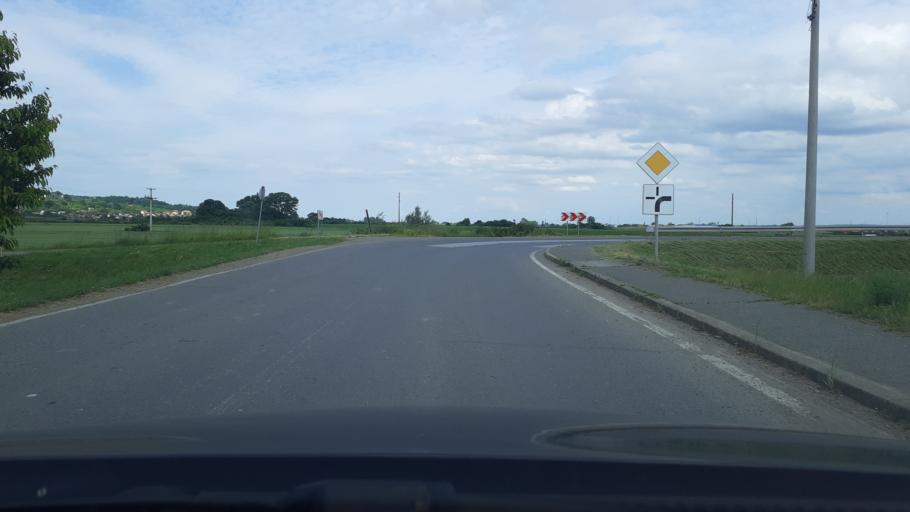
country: HR
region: Brodsko-Posavska
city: Slobodnica
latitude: 45.1729
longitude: 17.9303
